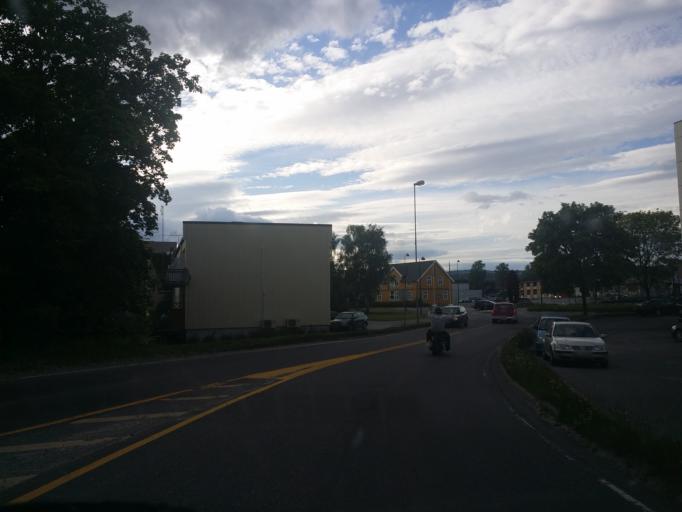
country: NO
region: Hedmark
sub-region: Ringsaker
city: Brumunddal
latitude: 60.8854
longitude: 10.9386
